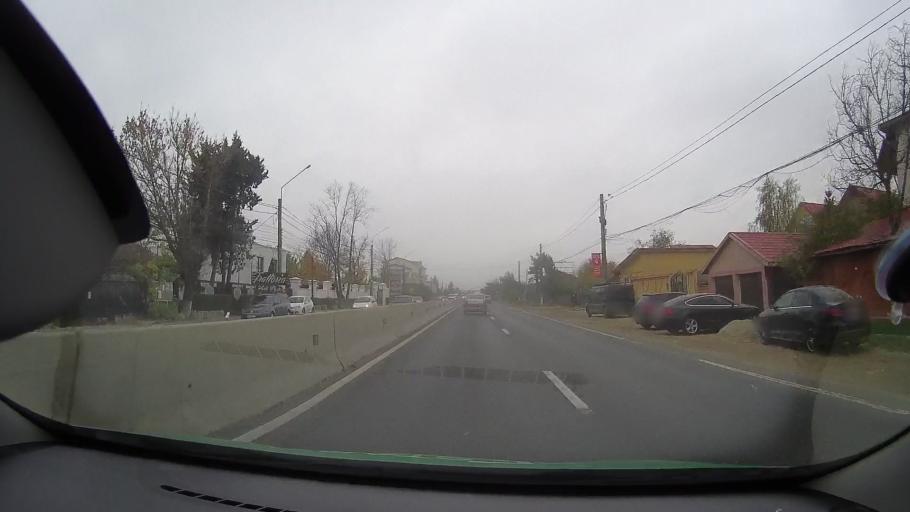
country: RO
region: Ilfov
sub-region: Comuna Corbeanca
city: Corbeanca
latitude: 44.6220
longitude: 26.0695
